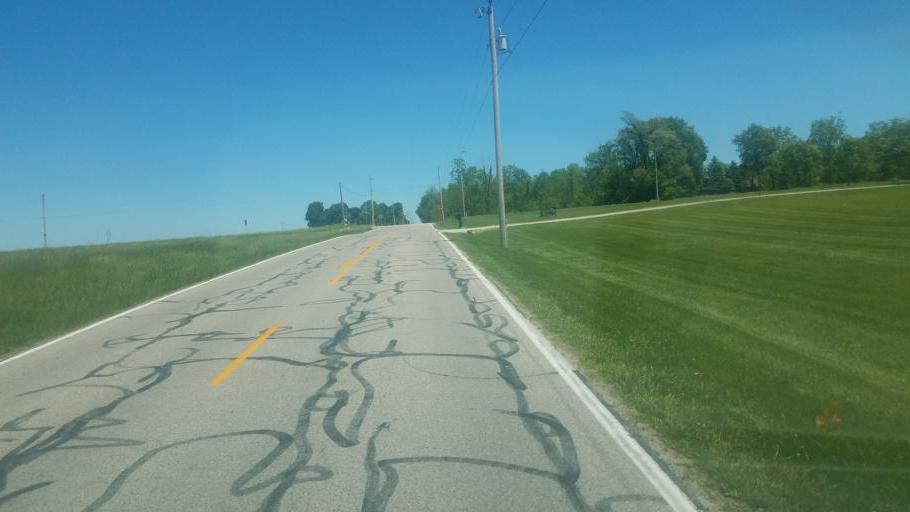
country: US
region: Ohio
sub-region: Shelby County
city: Sidney
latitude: 40.2142
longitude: -84.1641
